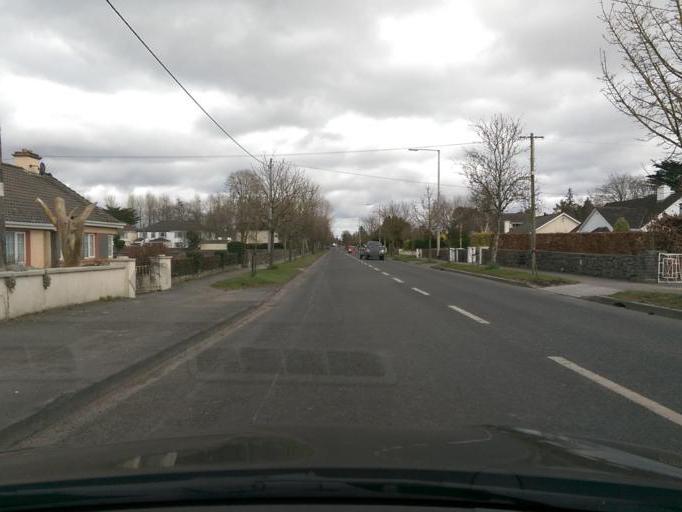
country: IE
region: Connaught
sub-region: County Galway
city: Ballinasloe
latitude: 53.3288
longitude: -8.1955
